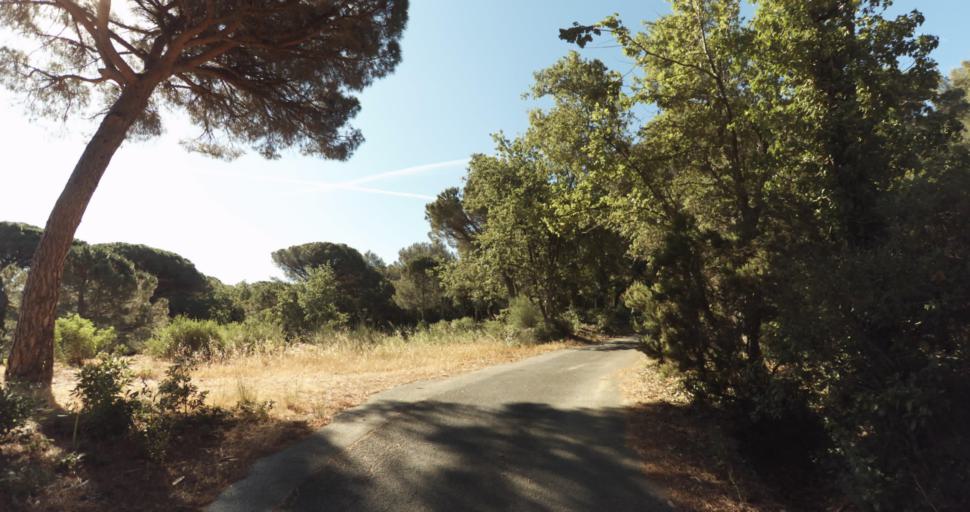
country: FR
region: Provence-Alpes-Cote d'Azur
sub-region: Departement du Var
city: Saint-Tropez
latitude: 43.2573
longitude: 6.6208
